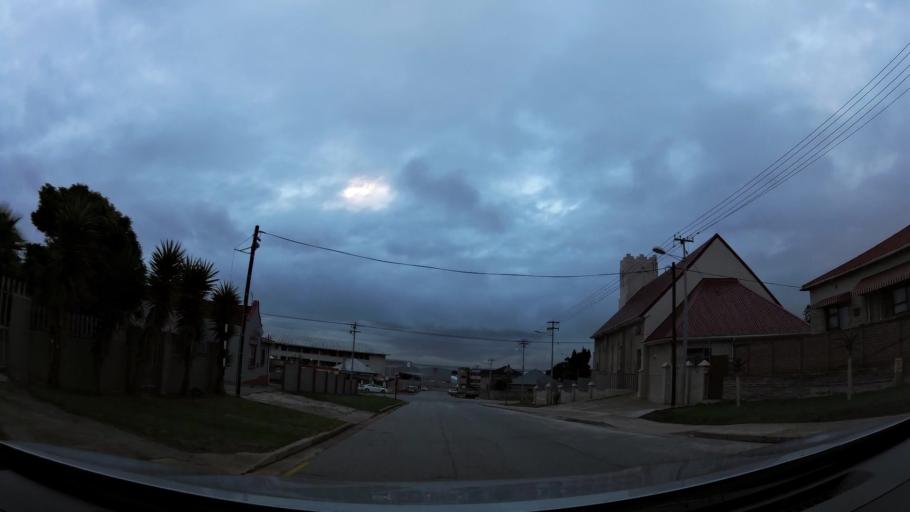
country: ZA
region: Eastern Cape
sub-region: Nelson Mandela Bay Metropolitan Municipality
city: Port Elizabeth
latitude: -33.9300
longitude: 25.5992
